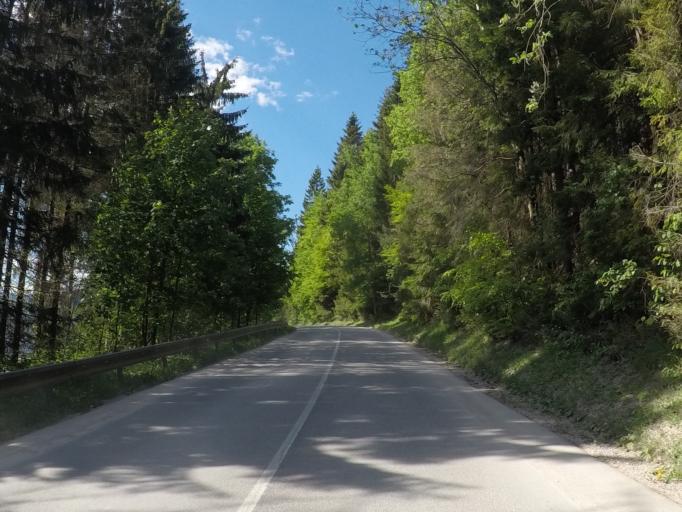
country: SK
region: Kosicky
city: Dobsina
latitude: 48.8547
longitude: 20.3859
